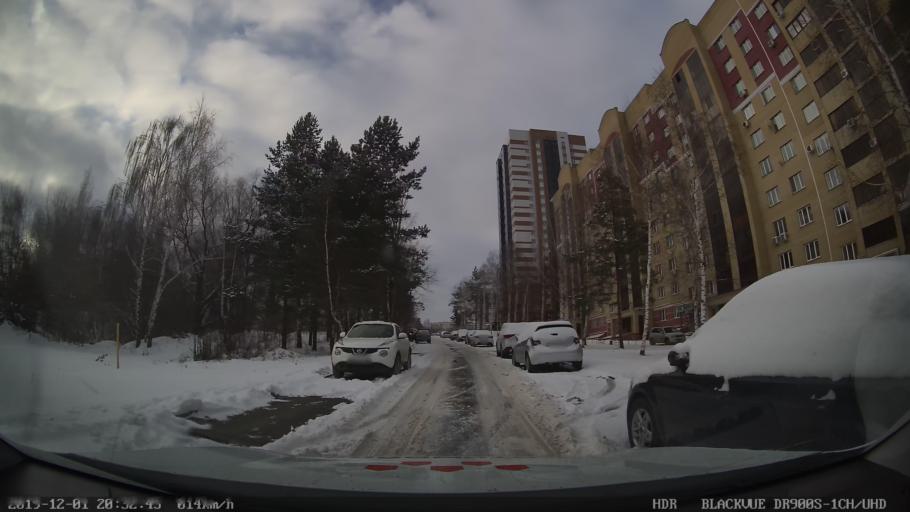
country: RU
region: Tatarstan
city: Stolbishchi
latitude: 55.7595
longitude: 49.2482
